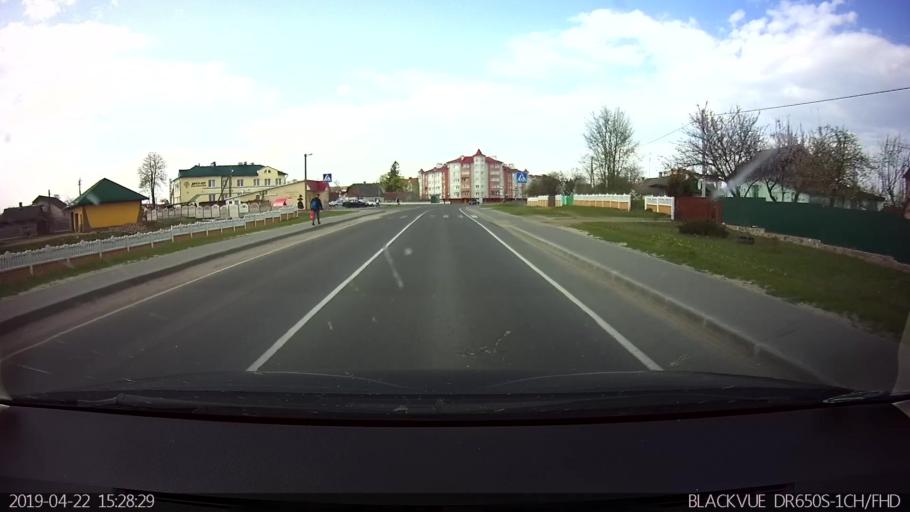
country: BY
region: Brest
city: Vysokaye
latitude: 52.3753
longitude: 23.3678
